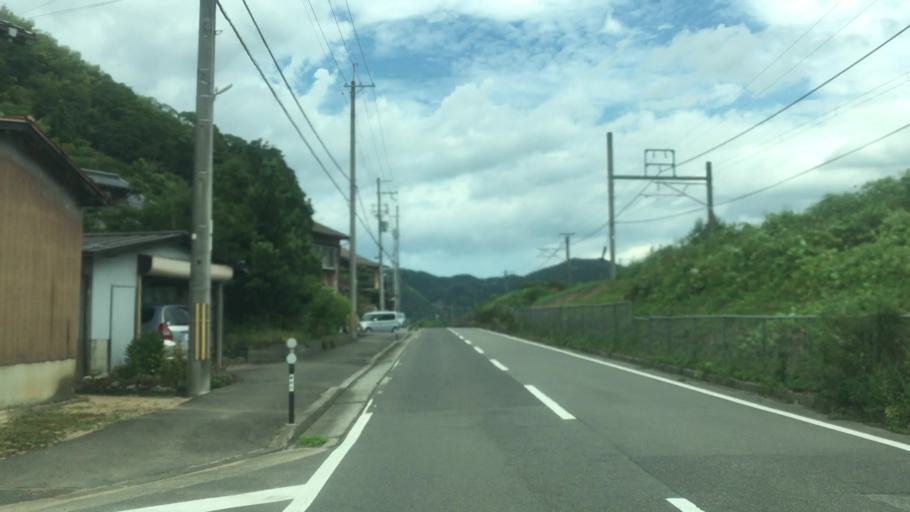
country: JP
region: Hyogo
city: Toyooka
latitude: 35.5663
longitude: 134.8035
